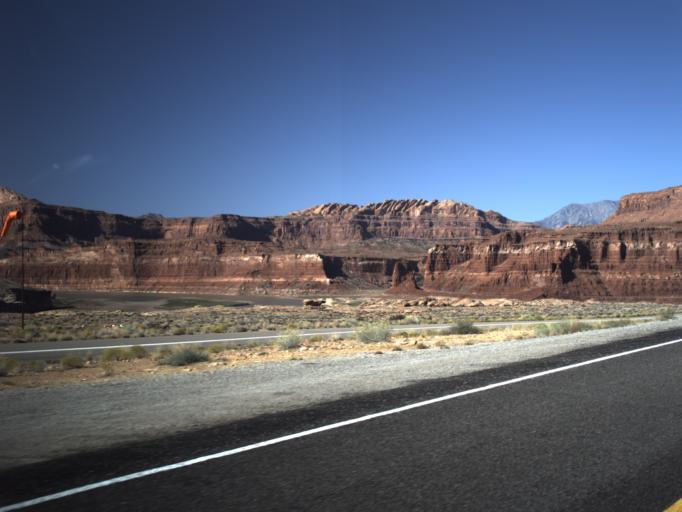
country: US
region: Utah
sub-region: San Juan County
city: Blanding
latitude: 37.8947
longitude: -110.3764
